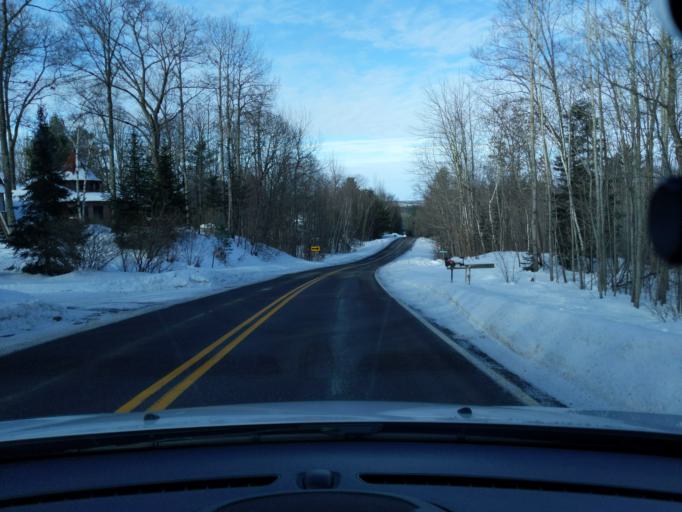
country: US
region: Wisconsin
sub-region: Sawyer County
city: Little Round Lake
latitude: 46.1177
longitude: -91.3402
